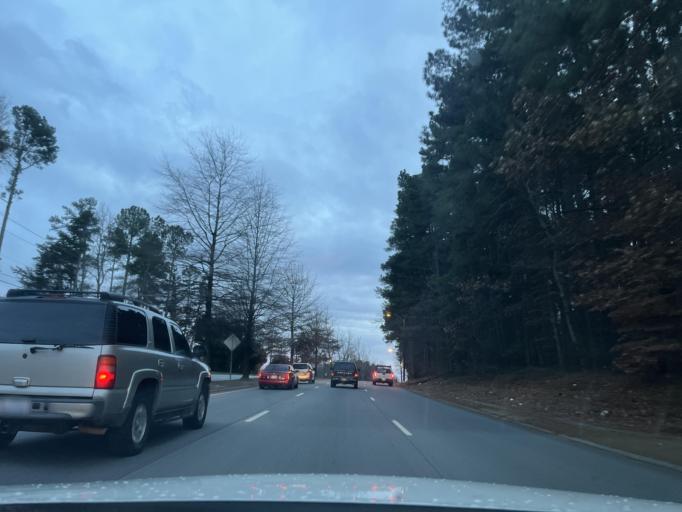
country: US
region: North Carolina
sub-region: Guilford County
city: Greensboro
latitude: 36.0294
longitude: -79.8483
